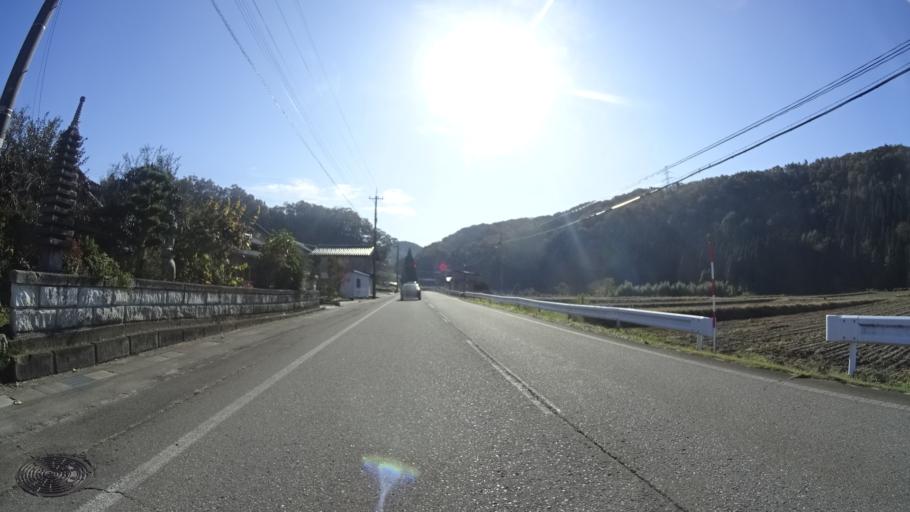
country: JP
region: Ishikawa
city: Komatsu
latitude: 36.3800
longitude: 136.5363
